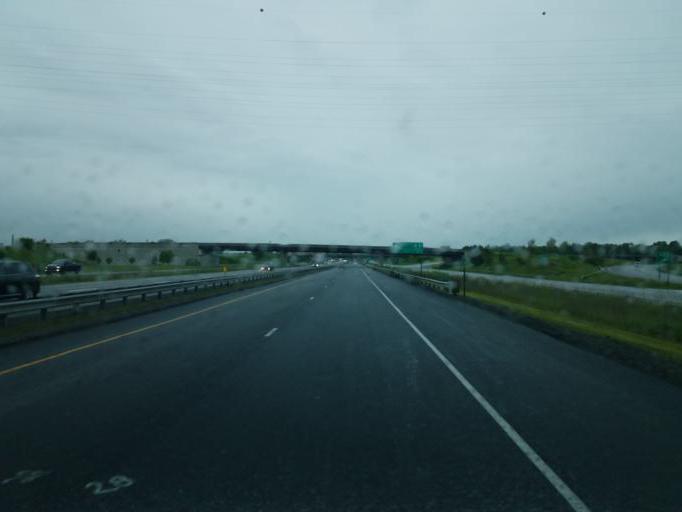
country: US
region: New York
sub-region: Oneida County
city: Utica
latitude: 43.1201
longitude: -75.2254
